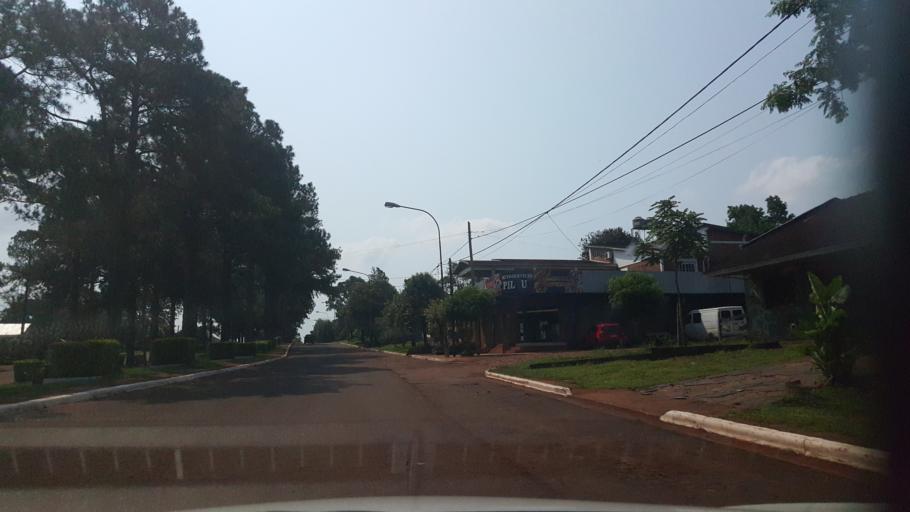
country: AR
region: Misiones
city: Santa Ana
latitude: -27.3749
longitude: -55.5773
